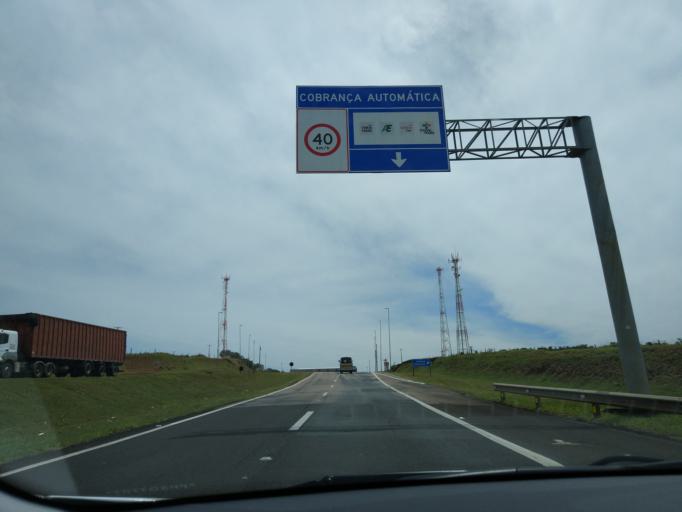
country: BR
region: Sao Paulo
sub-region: Botucatu
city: Botucatu
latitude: -22.8400
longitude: -48.5144
